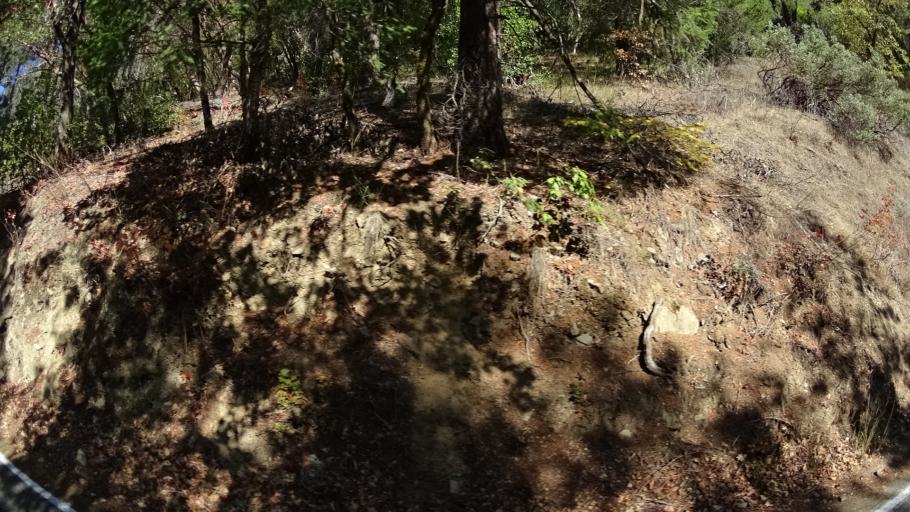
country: US
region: California
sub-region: Siskiyou County
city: Happy Camp
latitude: 41.3769
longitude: -123.4551
